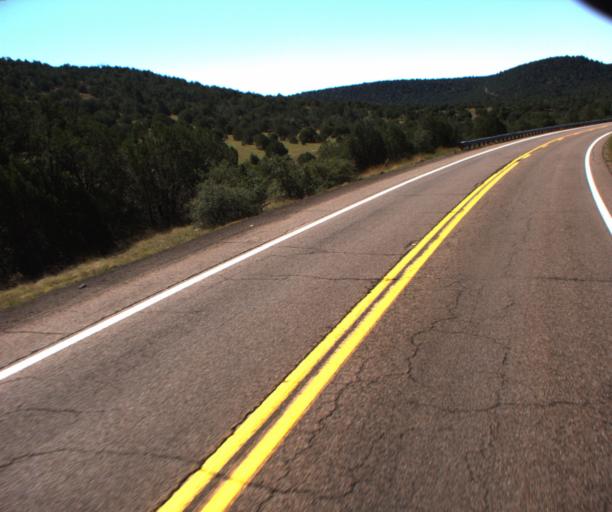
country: US
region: Arizona
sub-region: Navajo County
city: Cibecue
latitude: 33.9130
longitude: -110.3627
